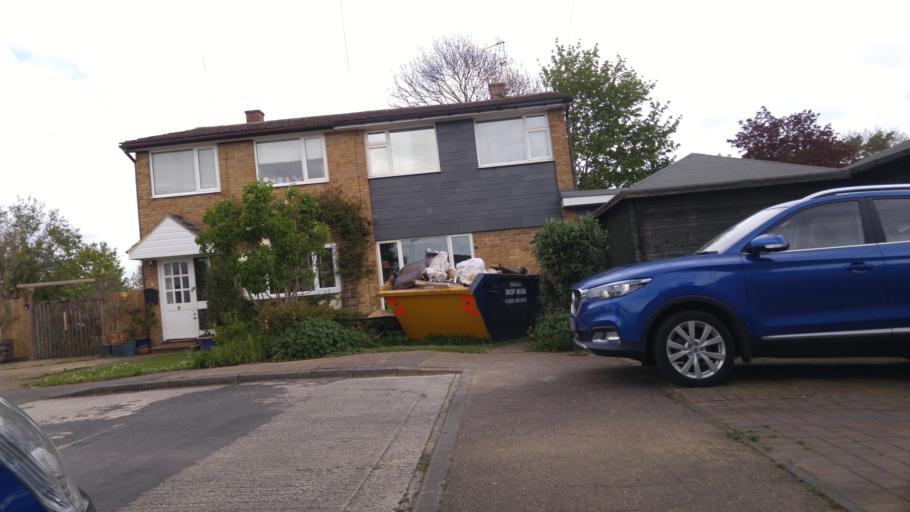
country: GB
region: England
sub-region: Essex
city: Earls Colne
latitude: 51.9429
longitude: 0.6933
